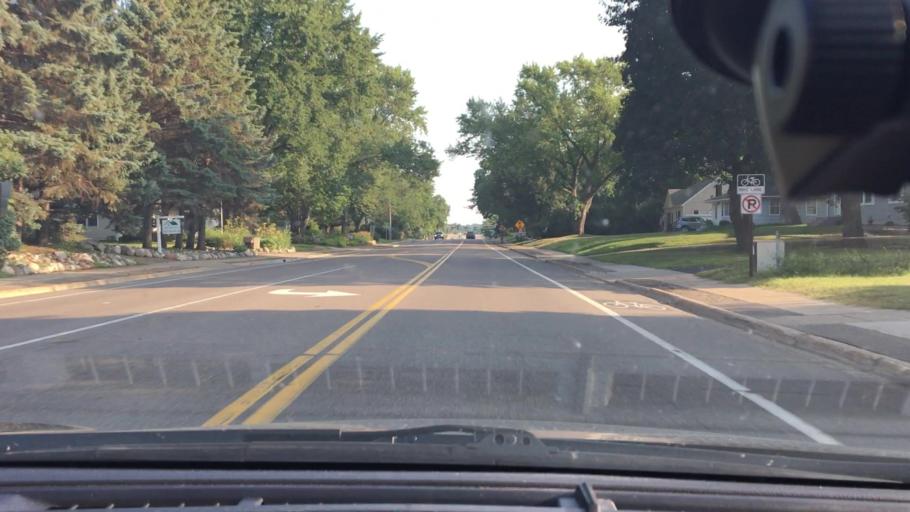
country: US
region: Minnesota
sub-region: Hennepin County
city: Golden Valley
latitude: 44.9926
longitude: -93.3805
